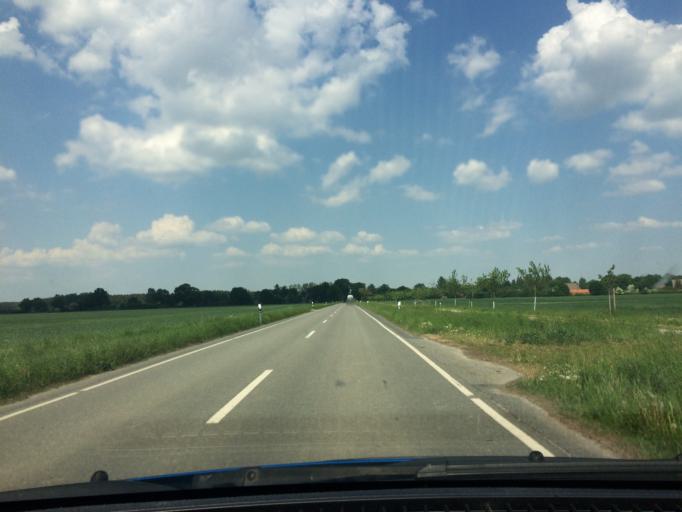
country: DE
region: Lower Saxony
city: Neu Darchau
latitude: 53.2545
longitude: 10.9110
